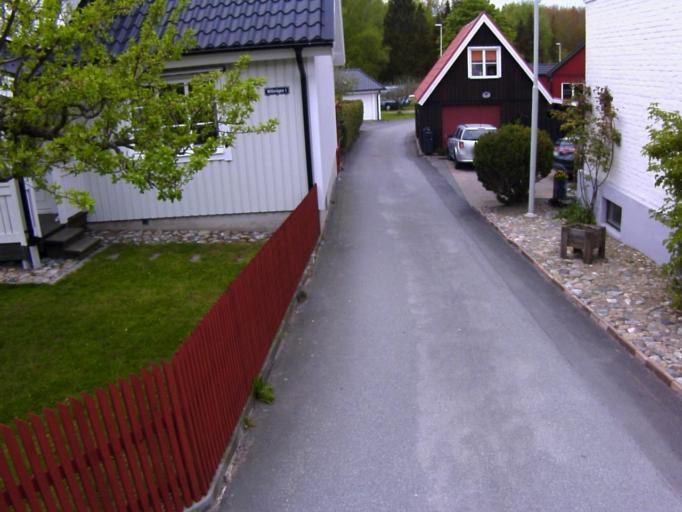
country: SE
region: Skane
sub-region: Kristianstads Kommun
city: Kristianstad
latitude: 56.0163
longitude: 14.1907
